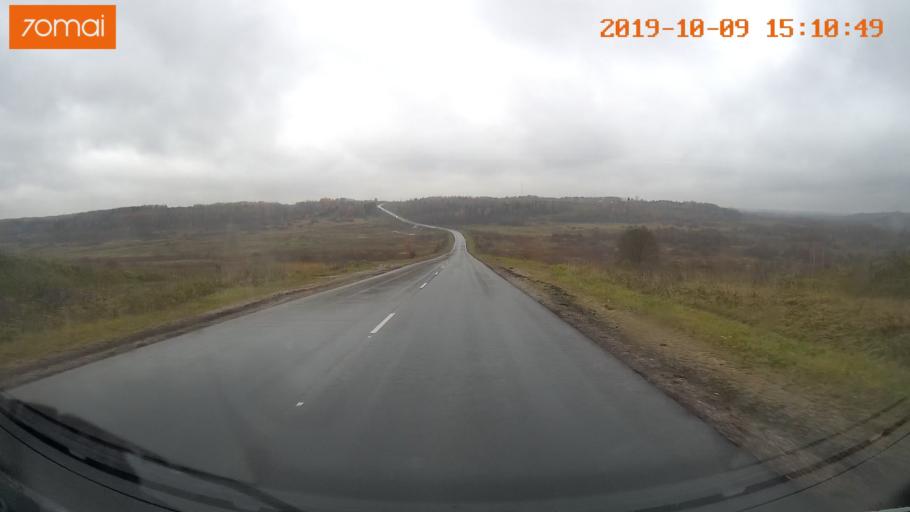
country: RU
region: Kostroma
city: Susanino
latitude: 58.1736
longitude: 41.6361
